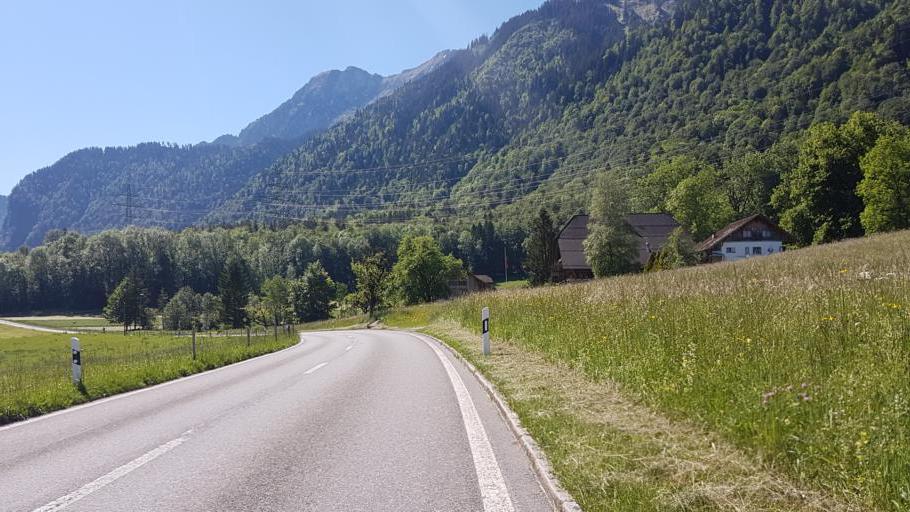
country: CH
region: Bern
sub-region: Thun District
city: Blumenstein
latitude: 46.7206
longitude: 7.5424
